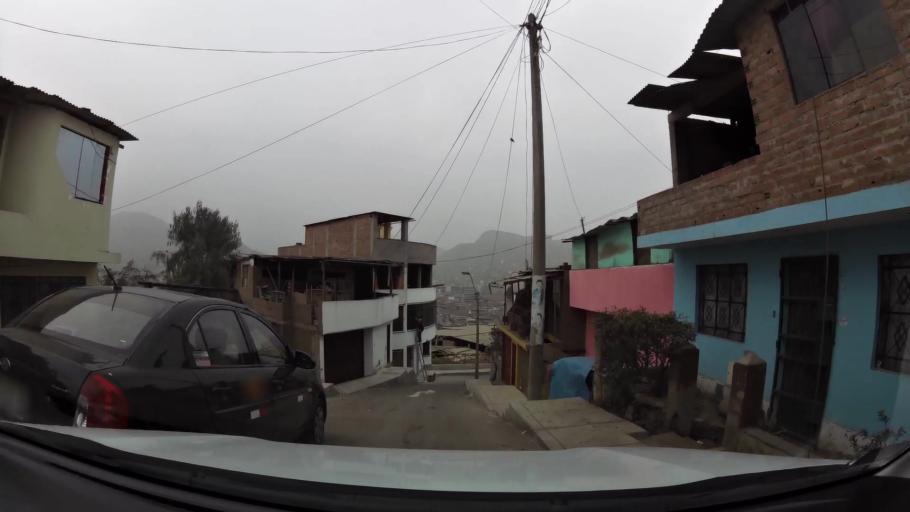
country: PE
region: Lima
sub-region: Lima
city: Surco
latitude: -12.1816
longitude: -76.9510
